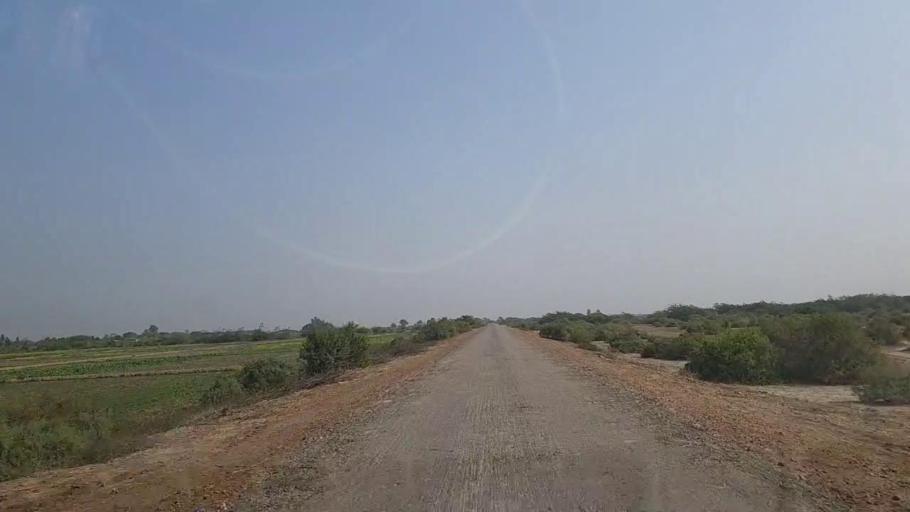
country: PK
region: Sindh
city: Keti Bandar
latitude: 24.2303
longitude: 67.6559
